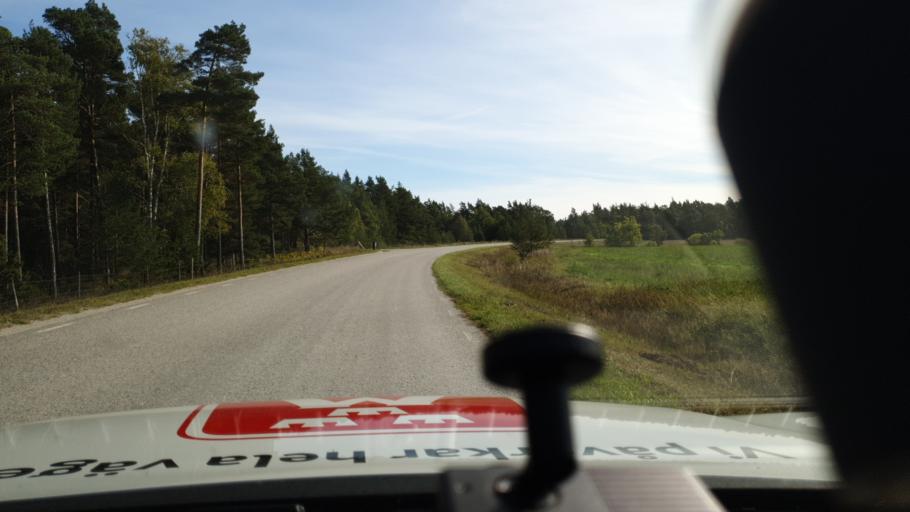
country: SE
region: Gotland
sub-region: Gotland
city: Slite
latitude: 57.8572
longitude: 18.7192
